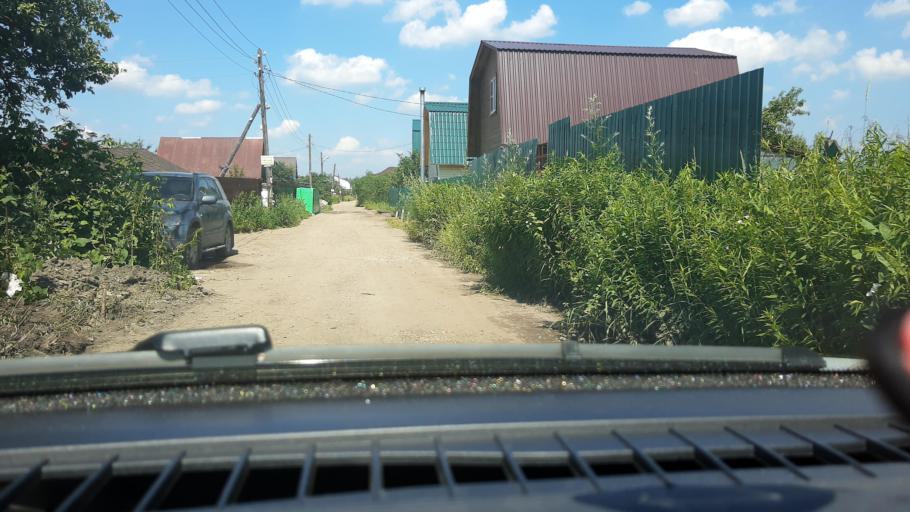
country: RU
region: Nizjnij Novgorod
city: Gorbatovka
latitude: 56.3148
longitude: 43.8302
